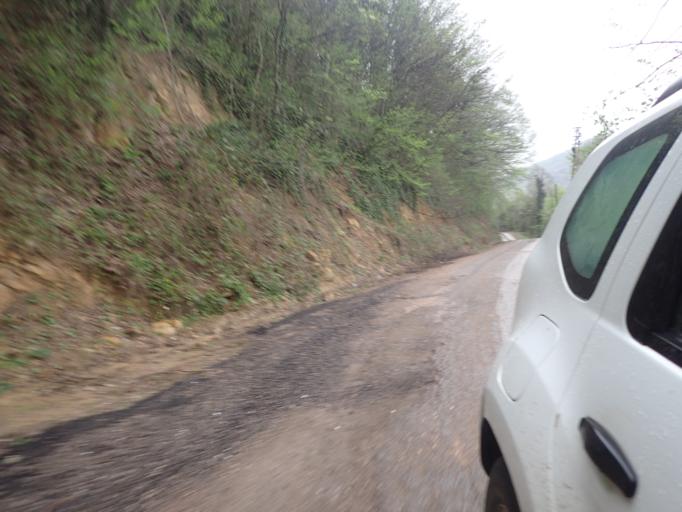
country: TR
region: Ordu
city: Korgan
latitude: 40.7778
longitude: 37.3458
